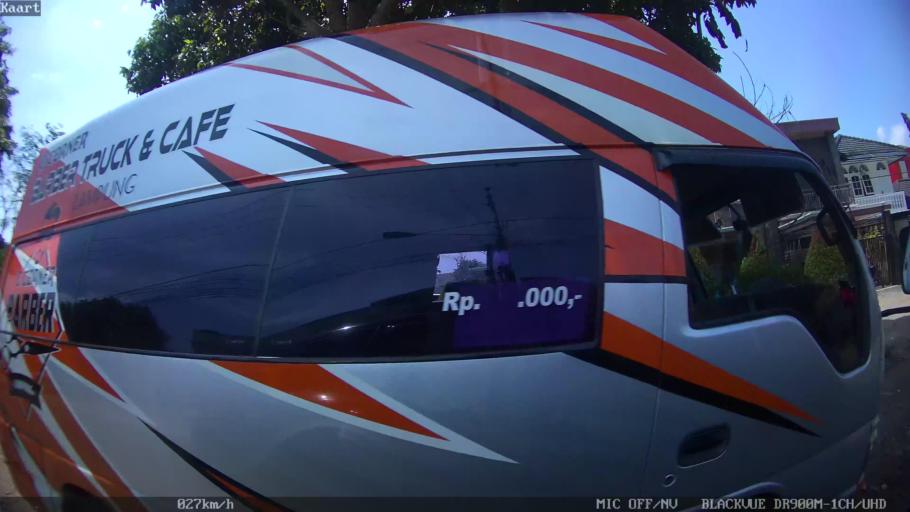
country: ID
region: Lampung
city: Kedaton
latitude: -5.3837
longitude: 105.2755
